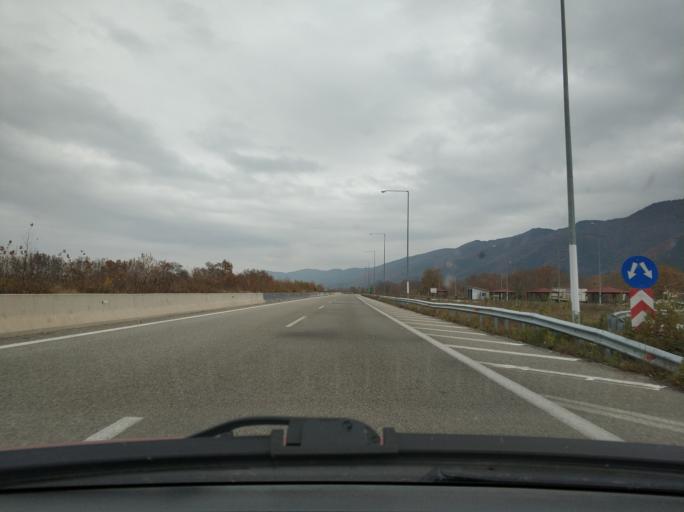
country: GR
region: East Macedonia and Thrace
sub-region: Nomos Kavalas
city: Eleftheres
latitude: 40.8631
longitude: 24.1780
